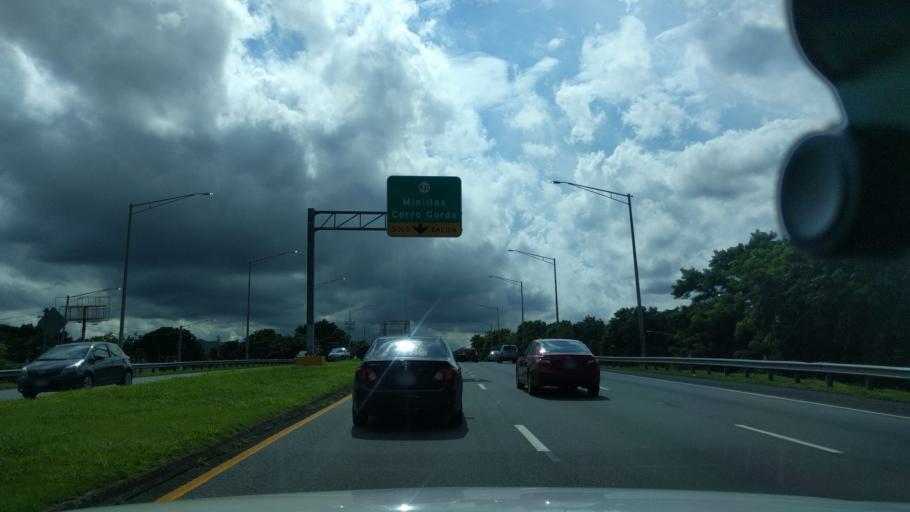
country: PR
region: Bayamon
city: Bayamon
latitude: 18.3704
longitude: -66.1658
